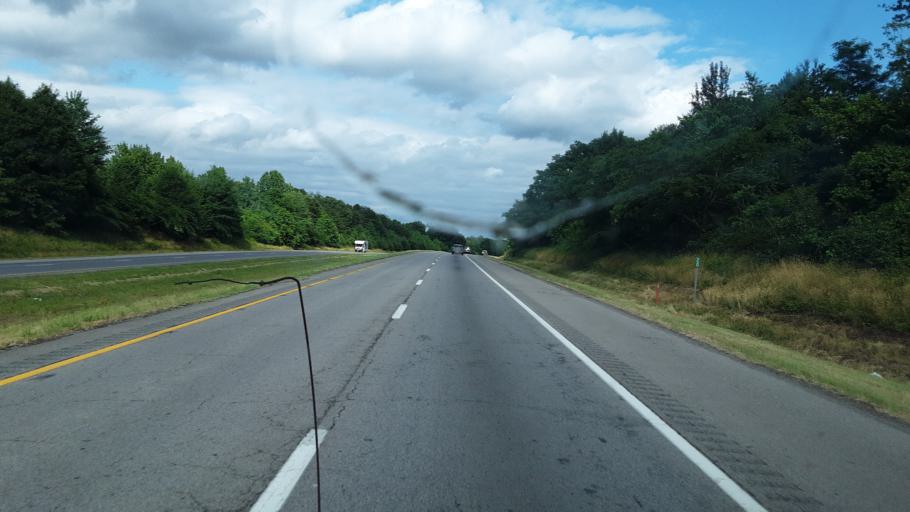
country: US
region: Virginia
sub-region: City of Danville
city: Danville
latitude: 36.5464
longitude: -79.4316
